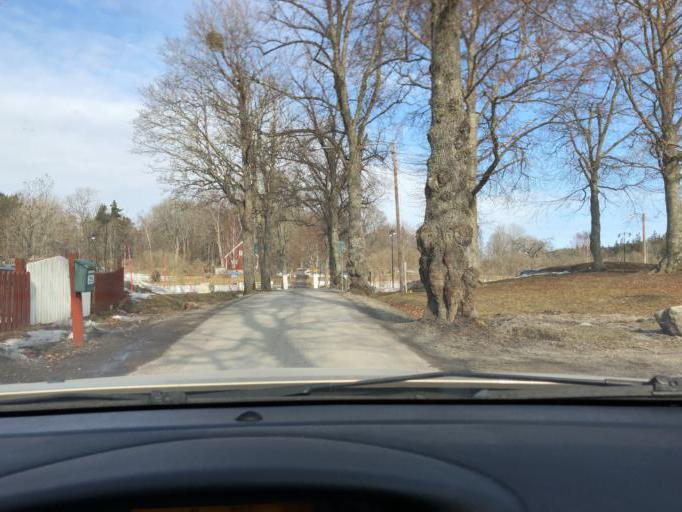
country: SE
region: Stockholm
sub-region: Nacka Kommun
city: Kummelnas
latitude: 59.3451
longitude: 18.3236
